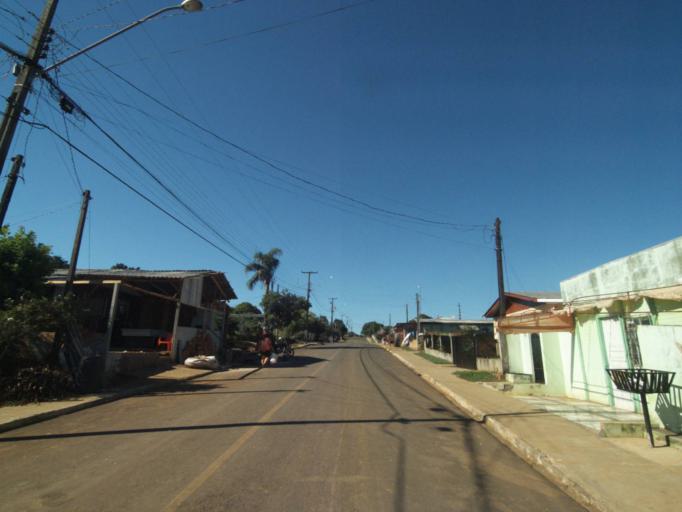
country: BR
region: Parana
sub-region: Pinhao
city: Pinhao
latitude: -25.8408
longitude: -52.0311
